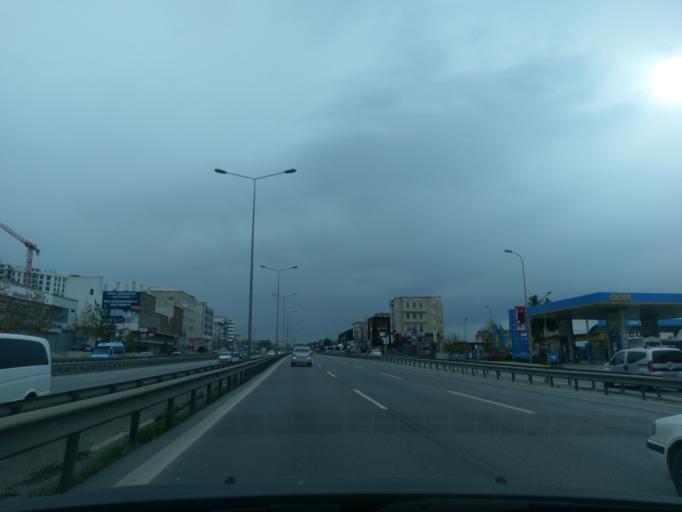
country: TR
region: Istanbul
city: Pendik
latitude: 40.8919
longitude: 29.2330
